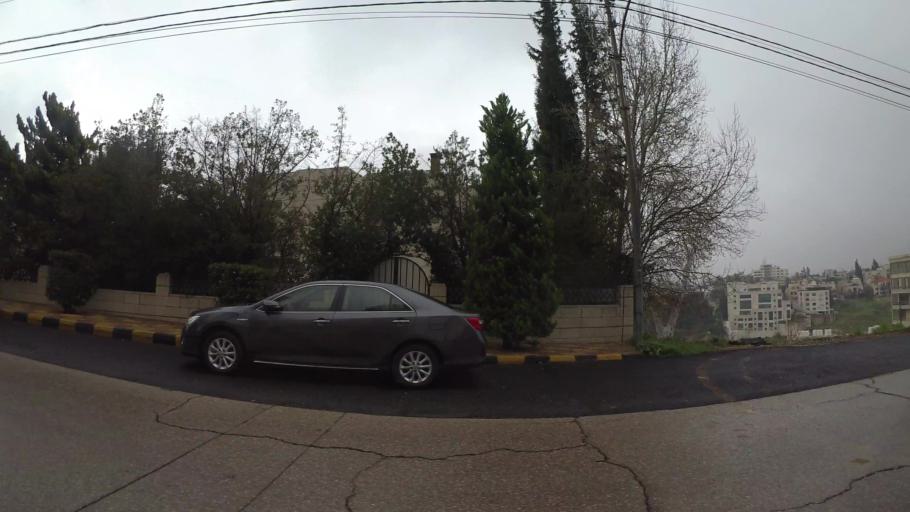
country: JO
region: Amman
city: Amman
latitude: 31.9534
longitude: 35.8945
